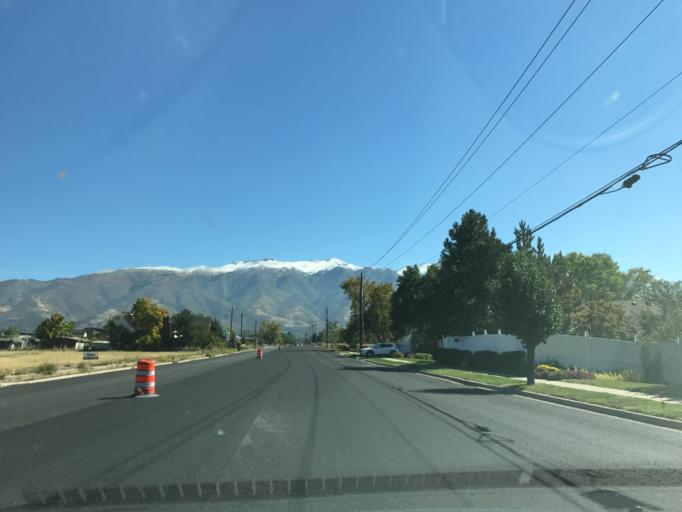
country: US
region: Utah
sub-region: Davis County
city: Hill Air Force Bace
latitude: 41.0892
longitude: -111.9659
